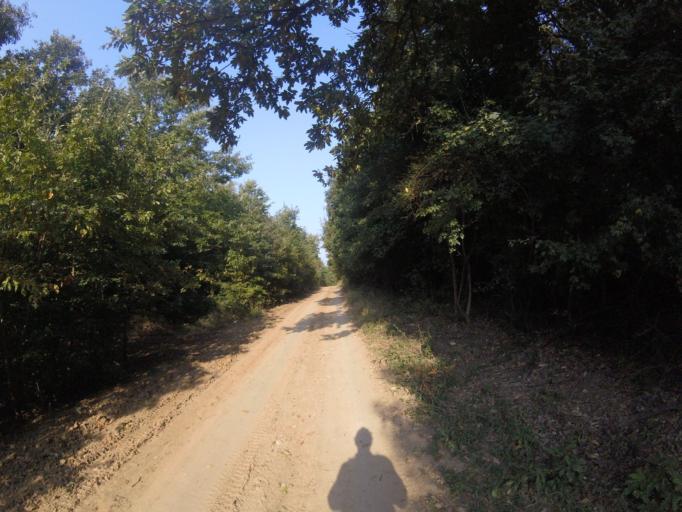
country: HU
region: Pest
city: Pilisszanto
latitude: 47.6840
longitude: 18.8561
